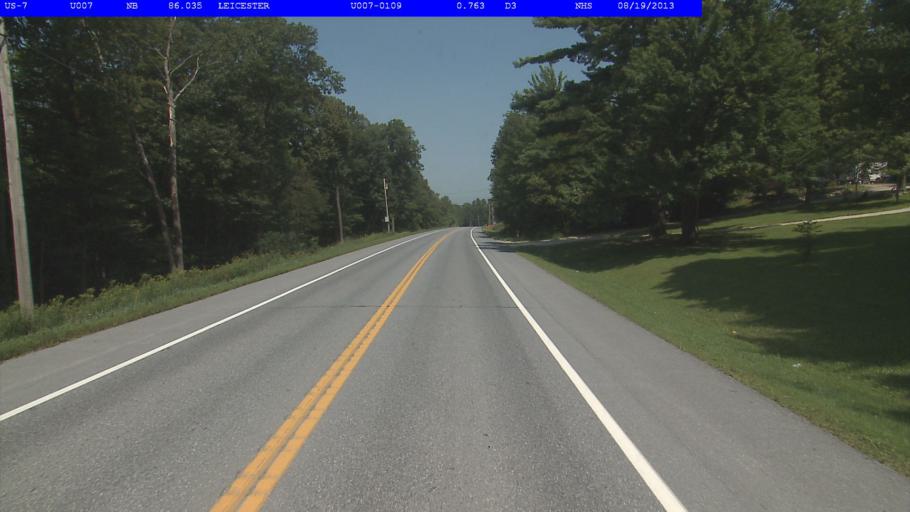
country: US
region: Vermont
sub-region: Rutland County
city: Brandon
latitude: 43.8543
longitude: -73.1063
